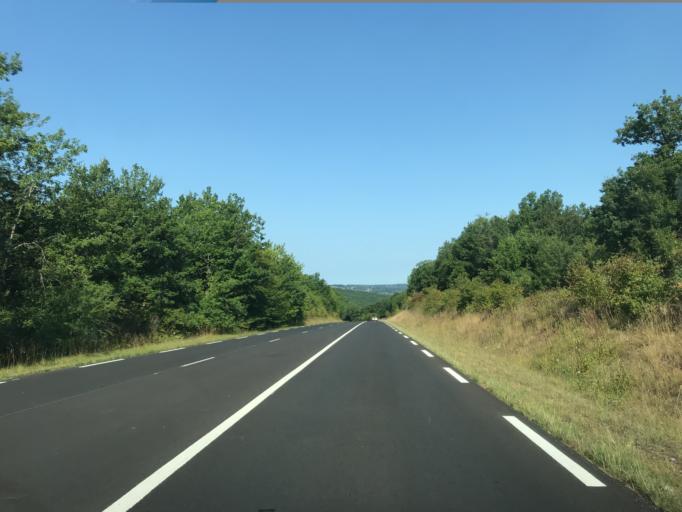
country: FR
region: Aquitaine
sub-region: Departement de la Dordogne
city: Montignac
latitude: 45.0473
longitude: 1.2212
